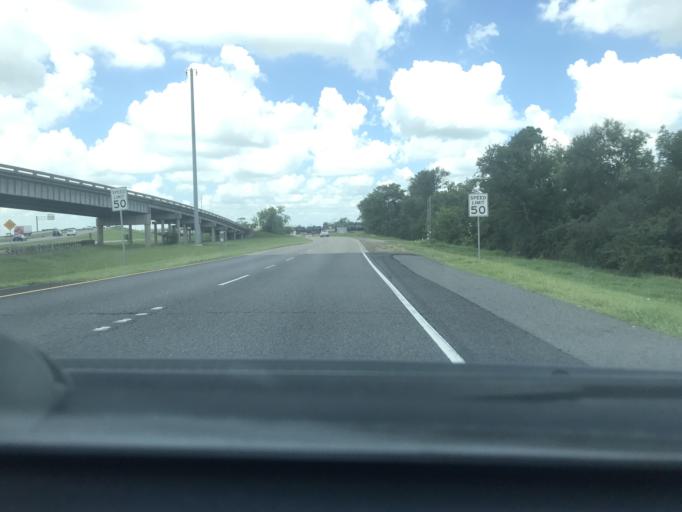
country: US
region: Louisiana
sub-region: Calcasieu Parish
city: Westlake
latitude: 30.2375
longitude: -93.2793
